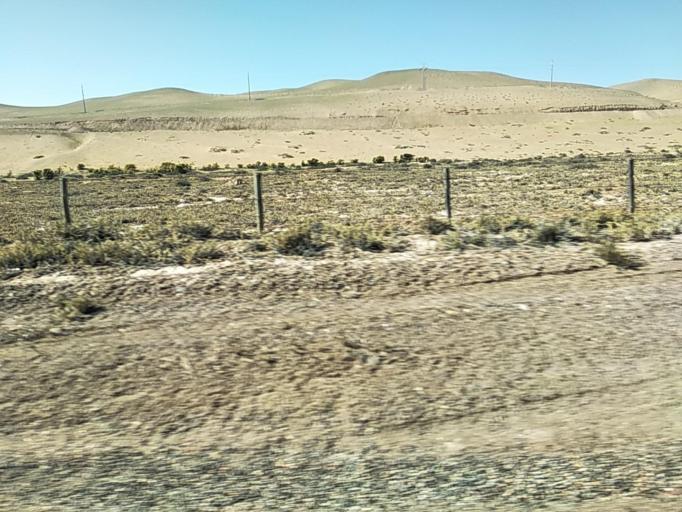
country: CL
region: Atacama
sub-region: Provincia de Copiapo
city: Copiapo
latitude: -27.3410
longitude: -70.7600
